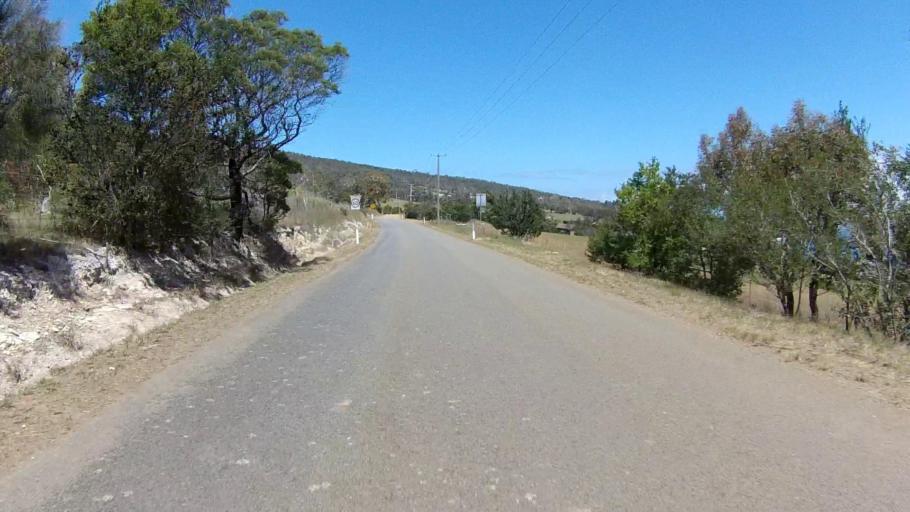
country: AU
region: Tasmania
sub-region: Clarence
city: Lauderdale
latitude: -42.9282
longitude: 147.4657
